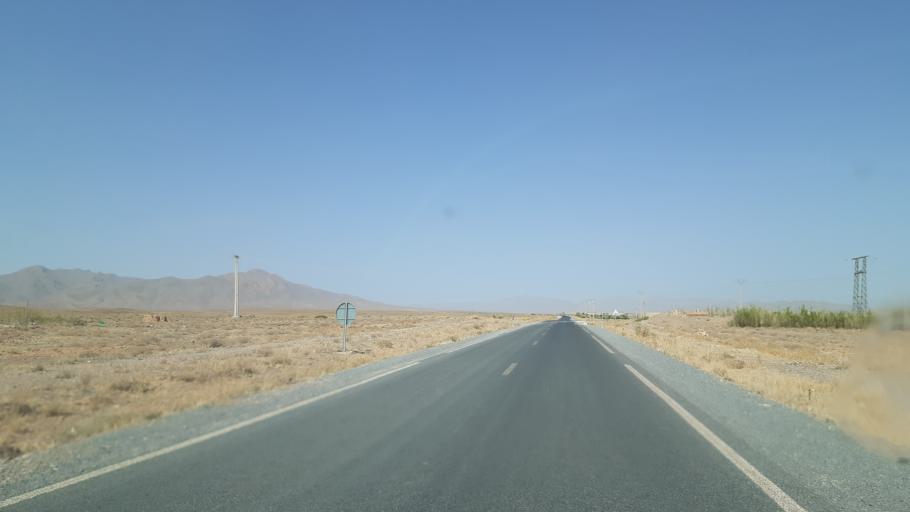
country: MA
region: Meknes-Tafilalet
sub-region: Errachidia
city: Amouguer
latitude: 32.2370
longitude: -4.6211
